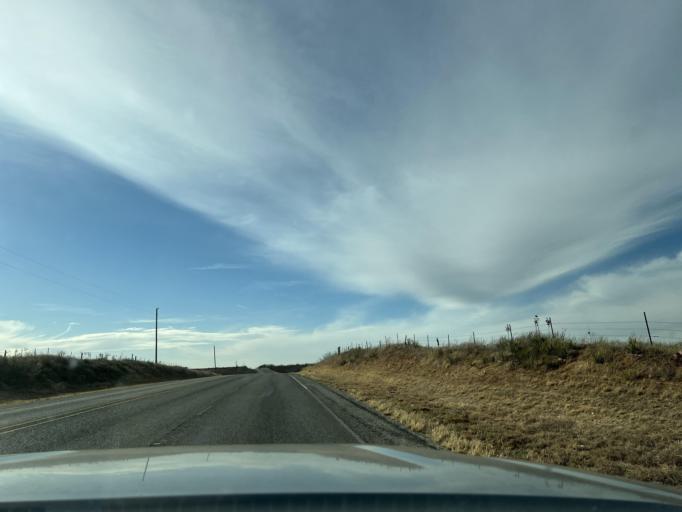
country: US
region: Texas
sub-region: Fisher County
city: Rotan
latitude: 32.7393
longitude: -100.5355
